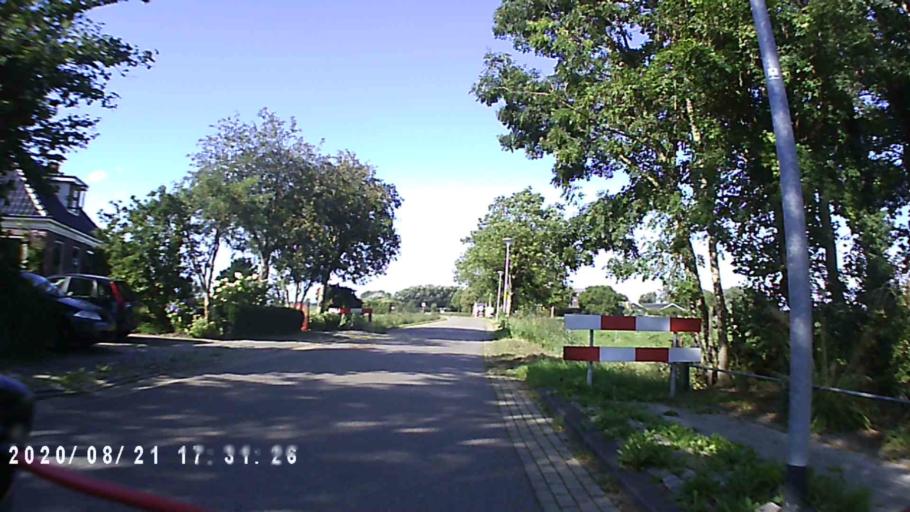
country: NL
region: Groningen
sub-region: Gemeente Bedum
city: Bedum
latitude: 53.2734
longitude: 6.5889
